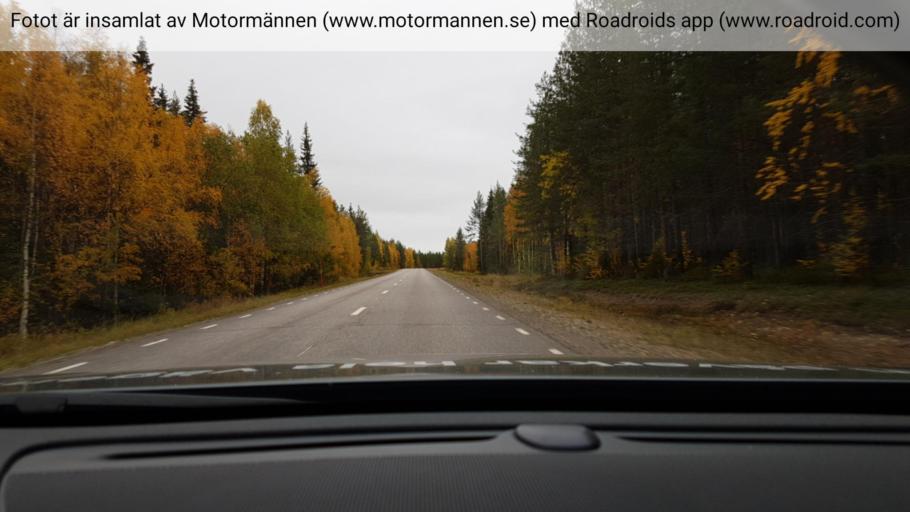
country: SE
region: Norrbotten
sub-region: Overkalix Kommun
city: OEverkalix
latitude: 66.5235
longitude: 22.7615
